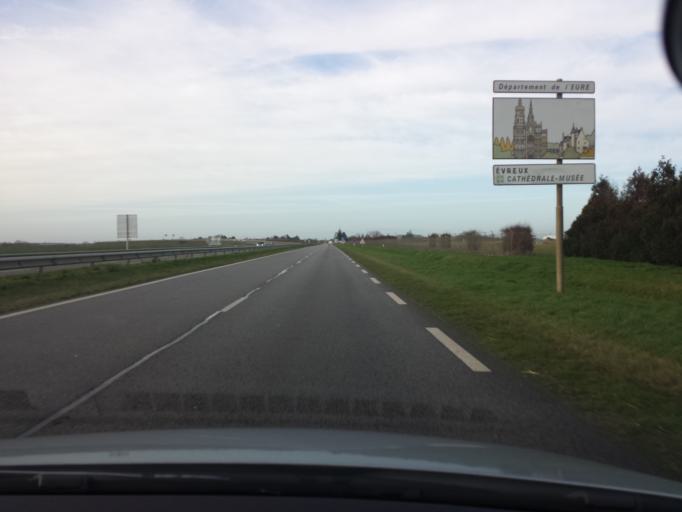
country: FR
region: Haute-Normandie
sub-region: Departement de l'Eure
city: Gravigny
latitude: 49.0149
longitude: 1.2071
